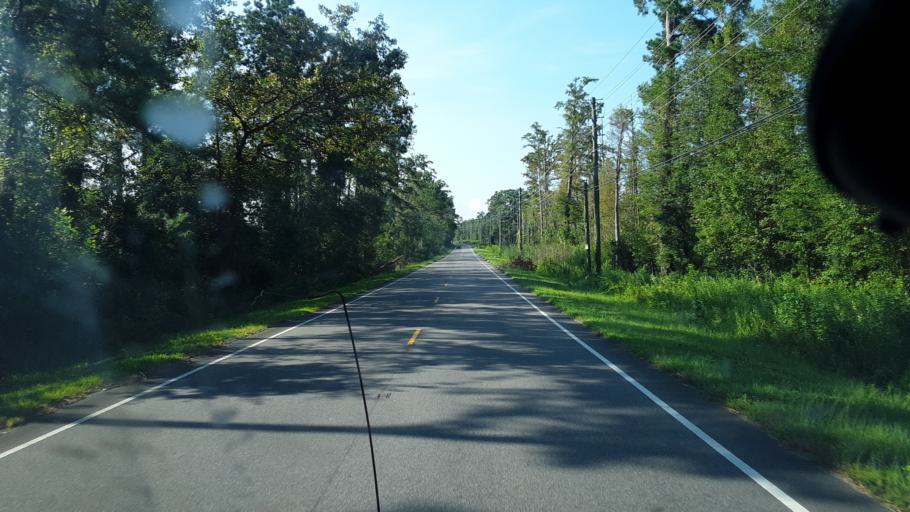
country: US
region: North Carolina
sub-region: Brunswick County
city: Belville
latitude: 34.1758
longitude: -77.9905
